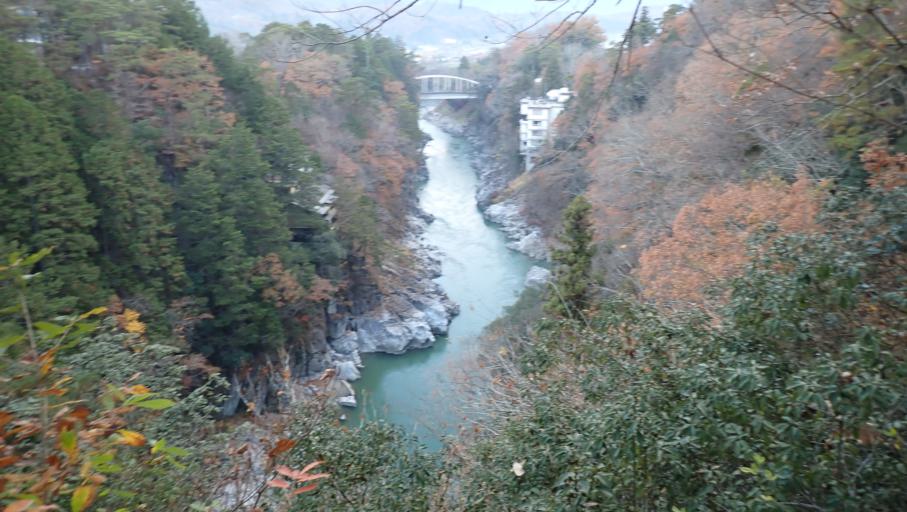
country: JP
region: Nagano
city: Iida
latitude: 35.4380
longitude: 137.8210
